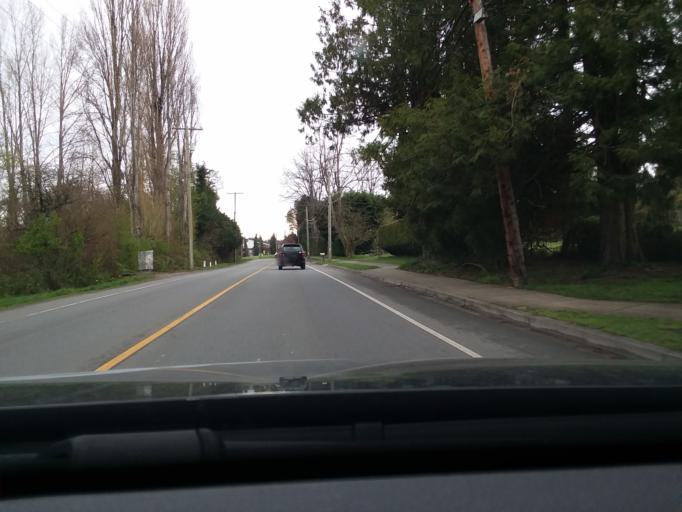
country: CA
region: British Columbia
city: North Saanich
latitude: 48.6280
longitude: -123.4203
